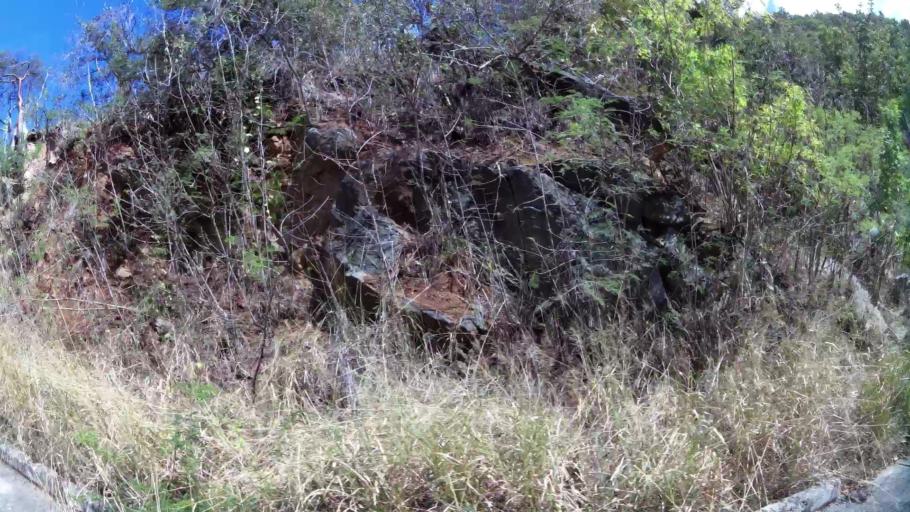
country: VG
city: Tortola
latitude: 18.4275
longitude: -64.5996
